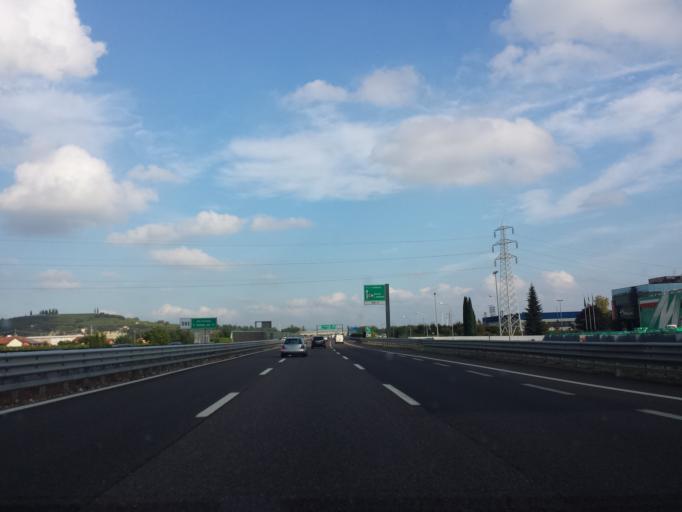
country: IT
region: Veneto
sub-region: Provincia di Verona
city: Soave
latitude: 45.4105
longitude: 11.2382
